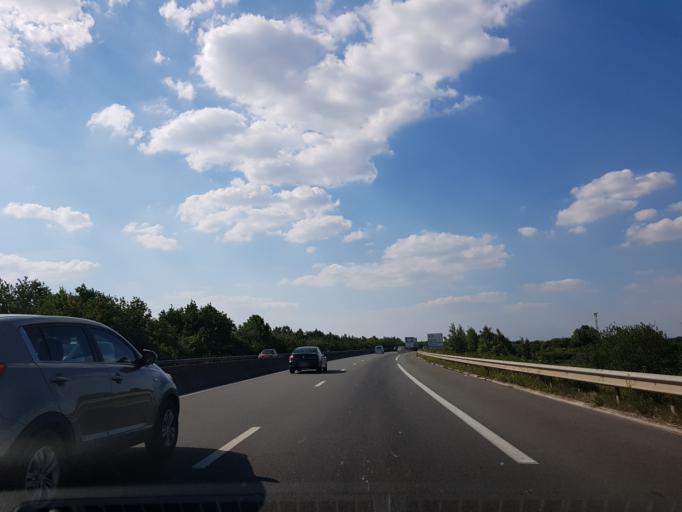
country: FR
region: Nord-Pas-de-Calais
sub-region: Departement du Nord
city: Somain
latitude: 50.3510
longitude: 3.2643
